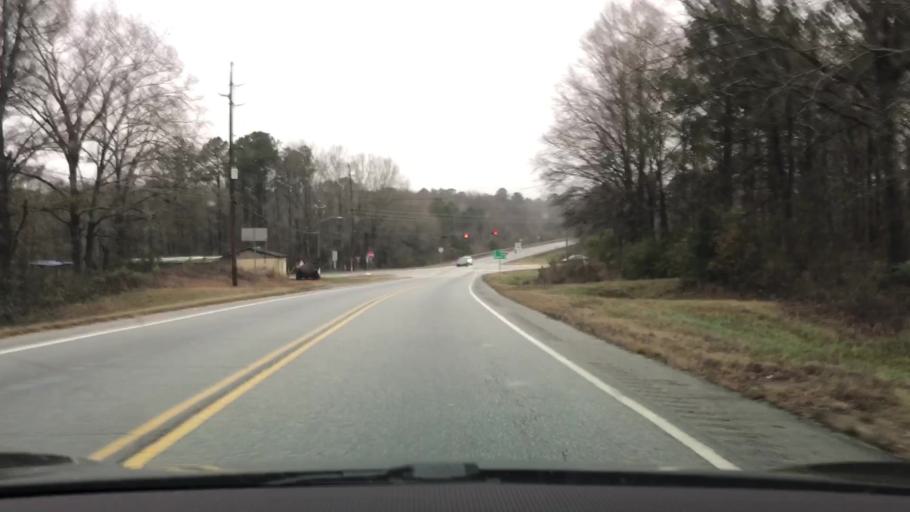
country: US
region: Georgia
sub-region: Warren County
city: Warrenton
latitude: 33.4021
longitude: -82.6690
